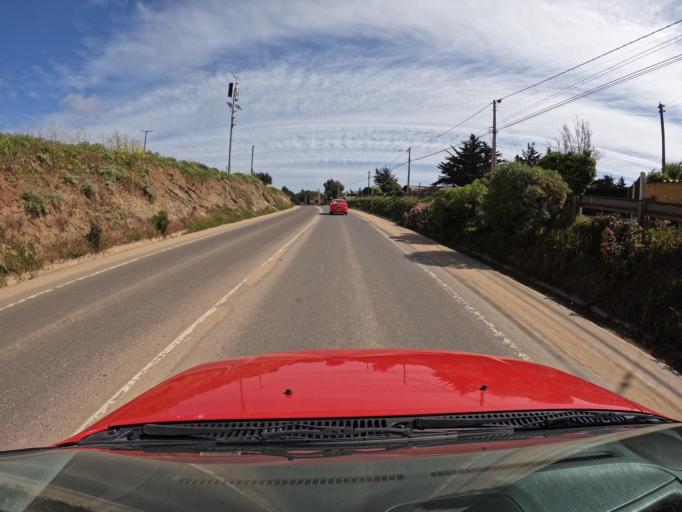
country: CL
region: O'Higgins
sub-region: Provincia de Colchagua
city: Santa Cruz
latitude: -34.4159
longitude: -72.0292
